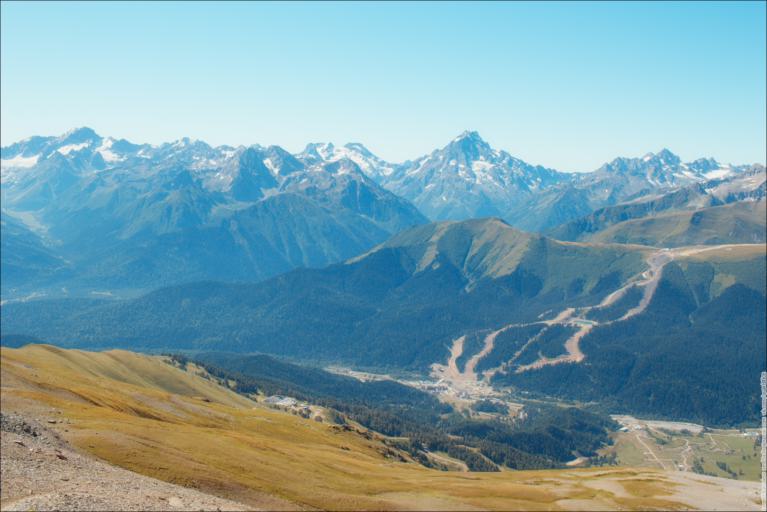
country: RU
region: Karachayevo-Cherkesiya
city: Nizhniy Arkhyz
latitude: 43.5878
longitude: 41.1861
